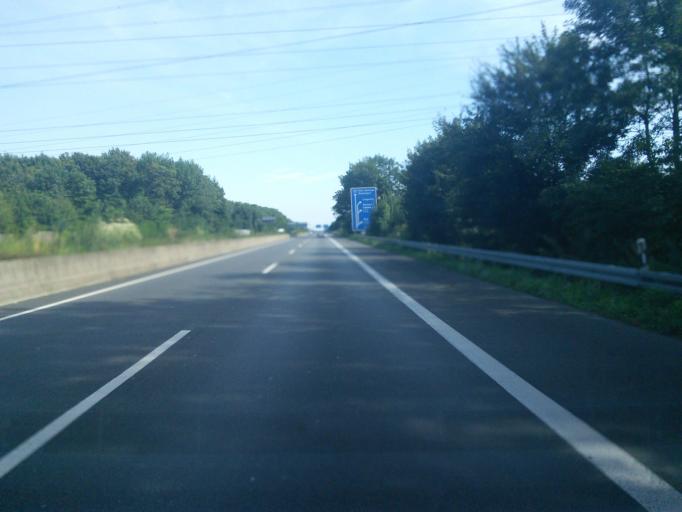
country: DE
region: North Rhine-Westphalia
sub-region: Regierungsbezirk Koln
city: Mengenich
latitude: 51.0062
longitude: 6.8790
